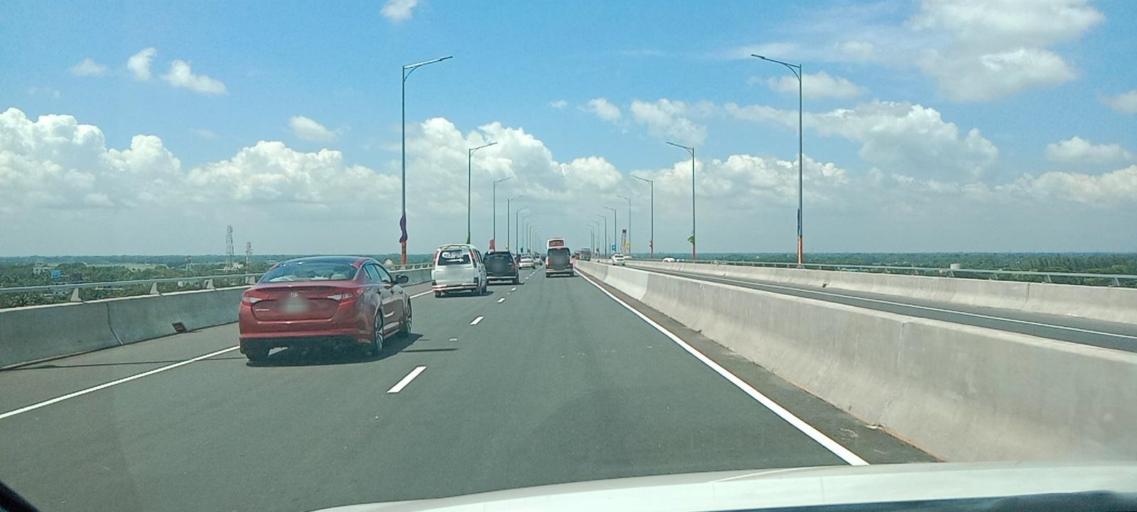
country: BD
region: Dhaka
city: Char Bhadrasan
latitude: 23.4681
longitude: 90.2640
